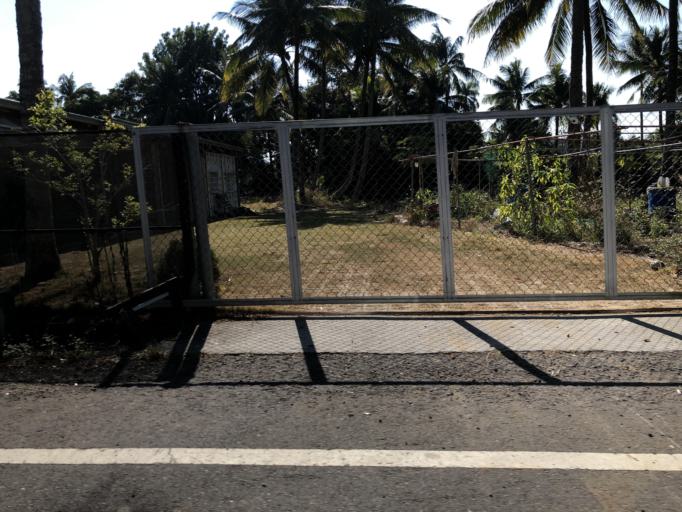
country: TW
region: Taiwan
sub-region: Tainan
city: Tainan
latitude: 23.0380
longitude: 120.3378
